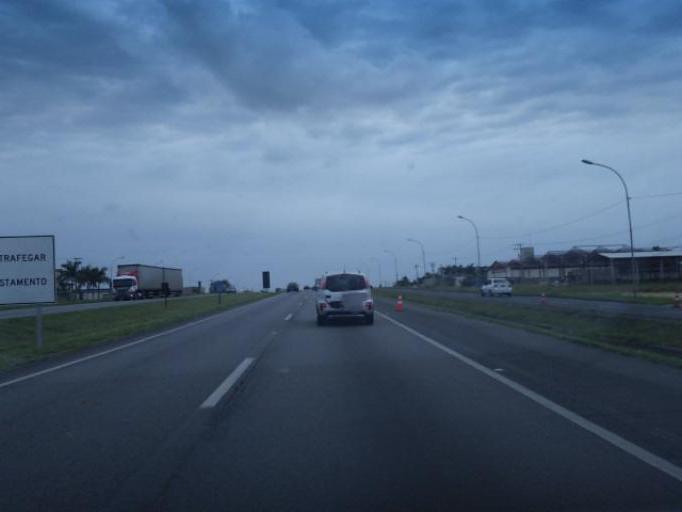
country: BR
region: Sao Paulo
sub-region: Registro
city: Registro
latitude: -24.5123
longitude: -47.8506
